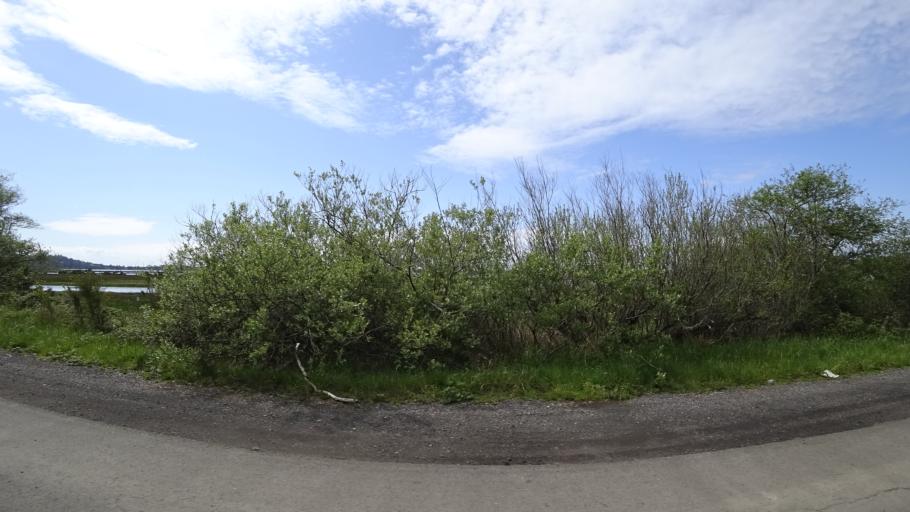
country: US
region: Oregon
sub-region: Lincoln County
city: Lincoln City
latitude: 44.9059
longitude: -124.0065
